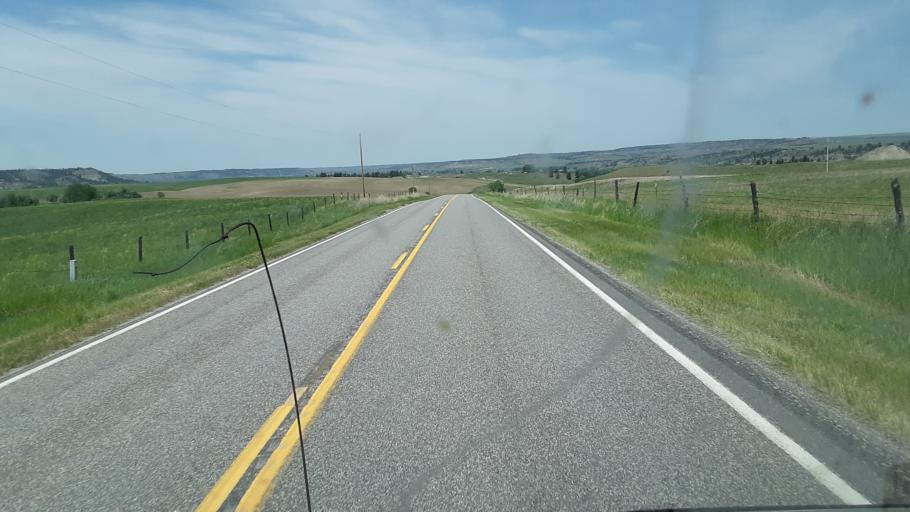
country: US
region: Montana
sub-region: Stillwater County
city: Columbus
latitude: 45.5927
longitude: -109.1949
